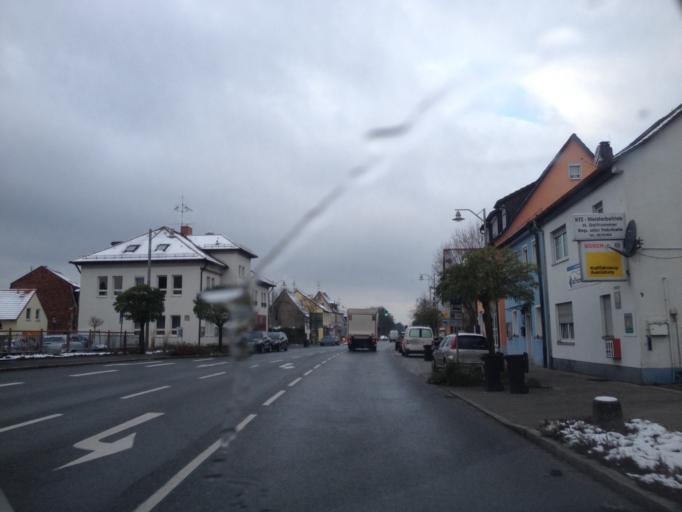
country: DE
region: Bavaria
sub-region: Regierungsbezirk Mittelfranken
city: Schwaig
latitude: 49.4803
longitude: 11.1999
